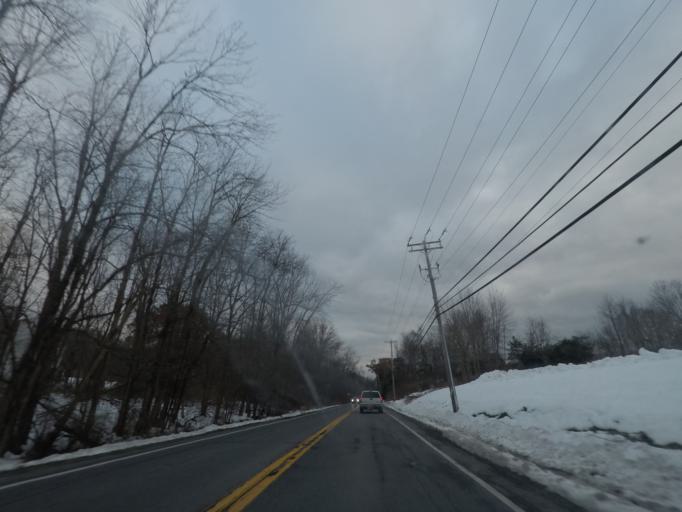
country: US
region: New York
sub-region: Orange County
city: Gardnertown
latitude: 41.5754
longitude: -74.0652
